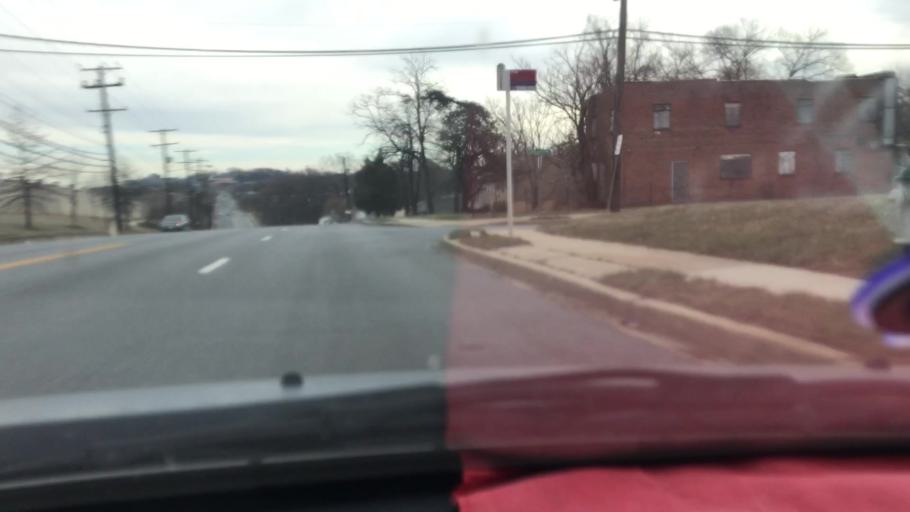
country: US
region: Maryland
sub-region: Prince George's County
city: Fairmount Heights
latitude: 38.9061
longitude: -76.9086
